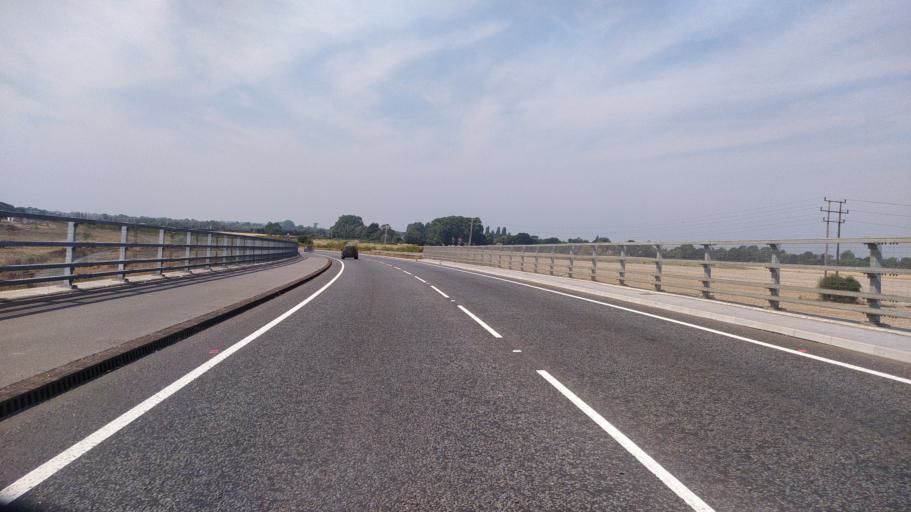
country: GB
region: England
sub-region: West Sussex
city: Barnham
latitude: 50.8098
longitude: -0.6582
